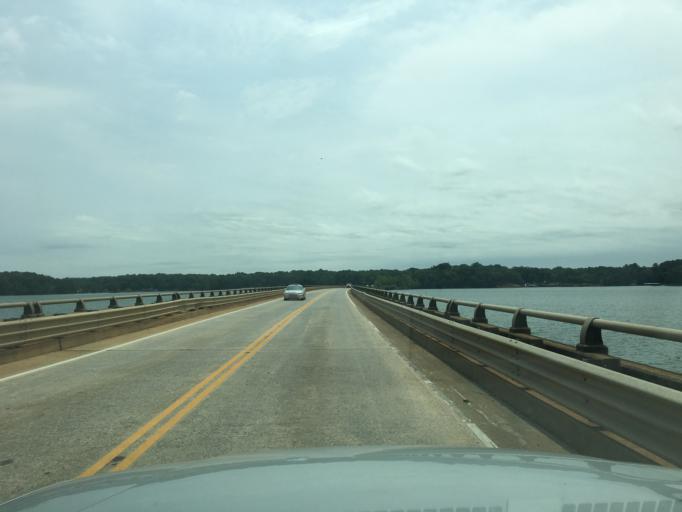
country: US
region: South Carolina
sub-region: Anderson County
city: Centerville
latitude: 34.5277
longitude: -82.7897
